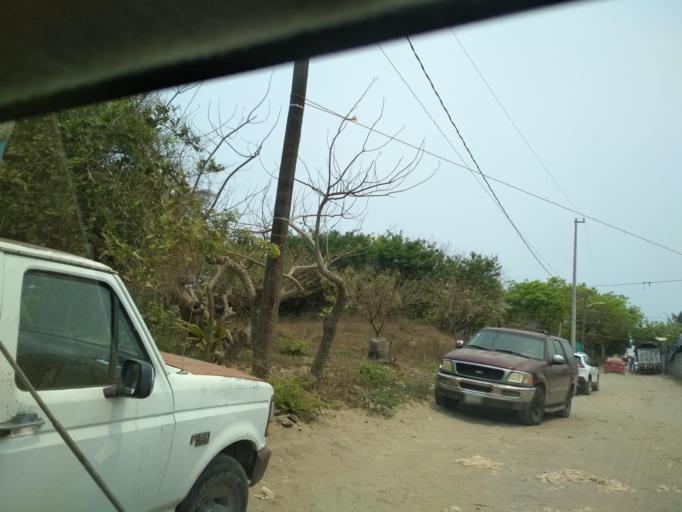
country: MX
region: Veracruz
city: Anton Lizardo
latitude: 19.0573
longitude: -95.9920
